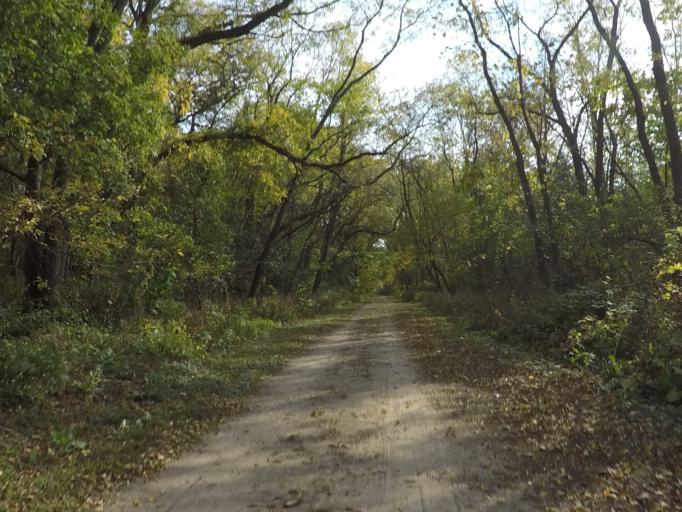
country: US
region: Wisconsin
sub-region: Dane County
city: Mount Horeb
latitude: 43.0146
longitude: -89.8128
